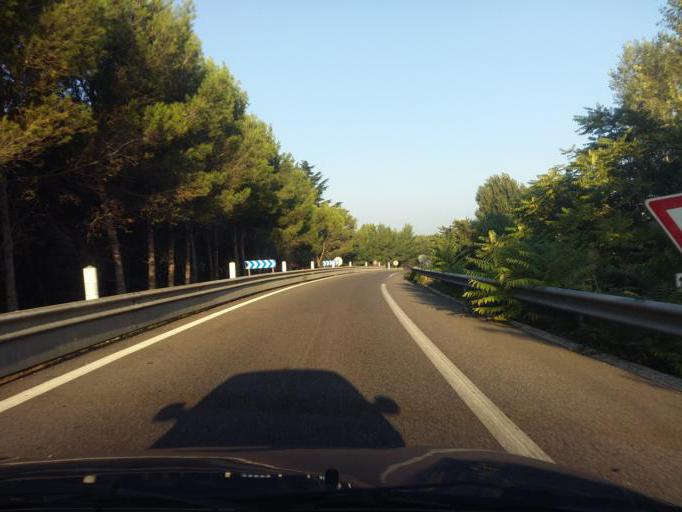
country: FR
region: Languedoc-Roussillon
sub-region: Departement du Gard
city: Nimes
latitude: 43.8113
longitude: 4.3471
